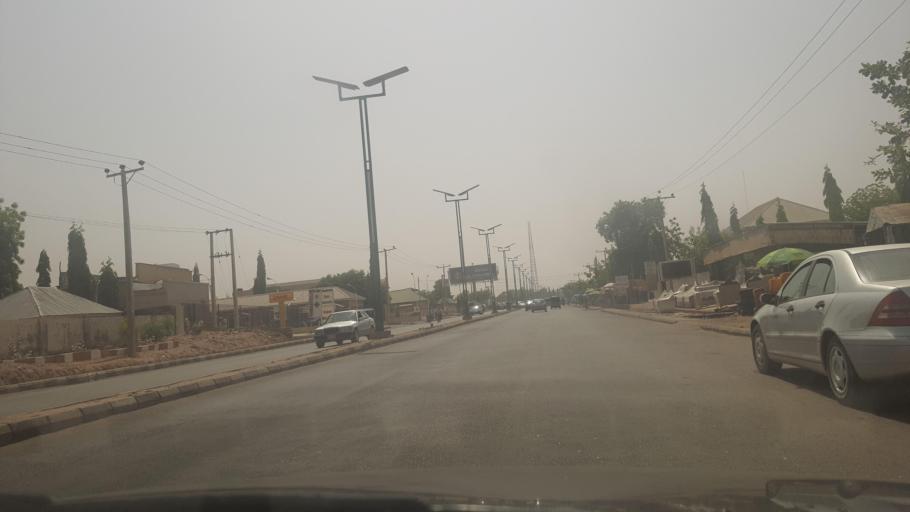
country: NG
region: Gombe
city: Gombe
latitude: 10.2862
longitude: 11.1399
